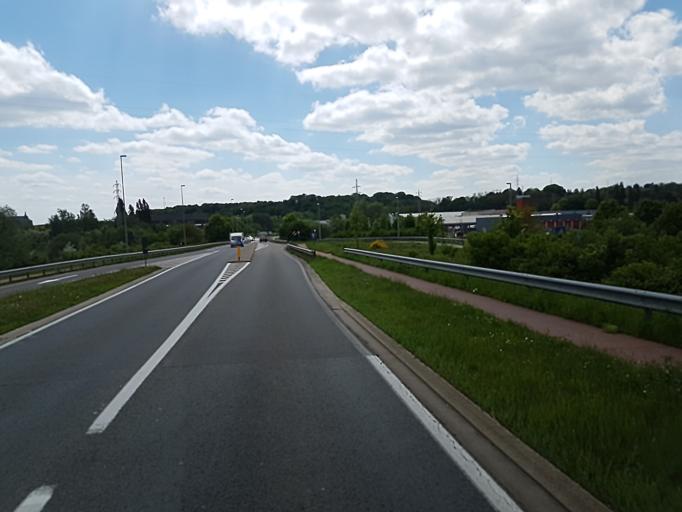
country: BE
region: Flanders
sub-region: Provincie Vlaams-Brabant
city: Diest
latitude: 50.9927
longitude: 5.0408
